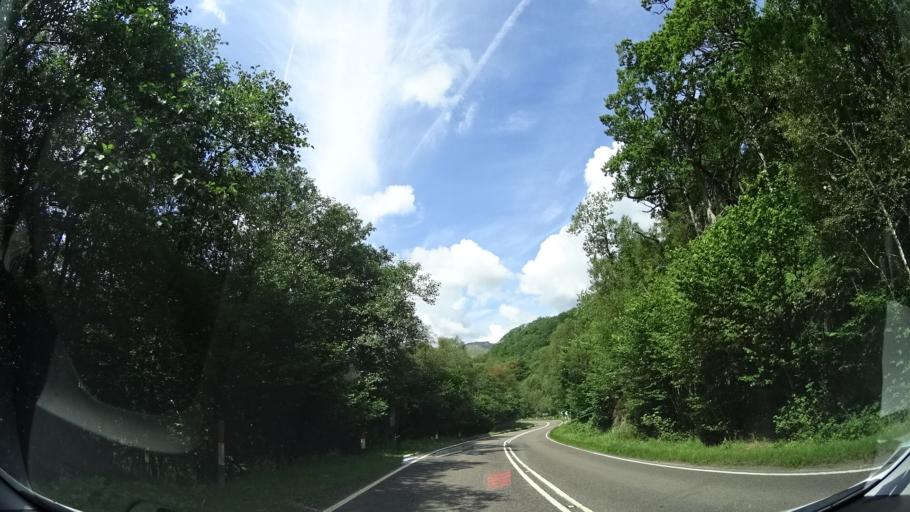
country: GB
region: Scotland
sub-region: Highland
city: Fort William
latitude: 56.8647
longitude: -5.4157
